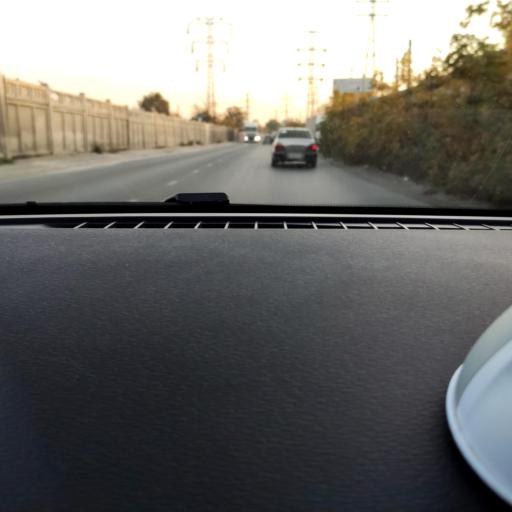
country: RU
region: Samara
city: Petra-Dubrava
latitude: 53.2468
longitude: 50.2927
